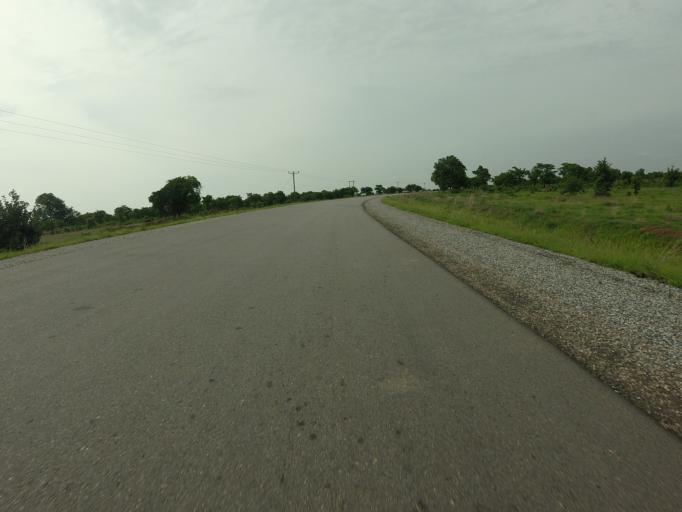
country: GH
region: Northern
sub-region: Yendi
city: Yendi
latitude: 9.8278
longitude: -0.1220
